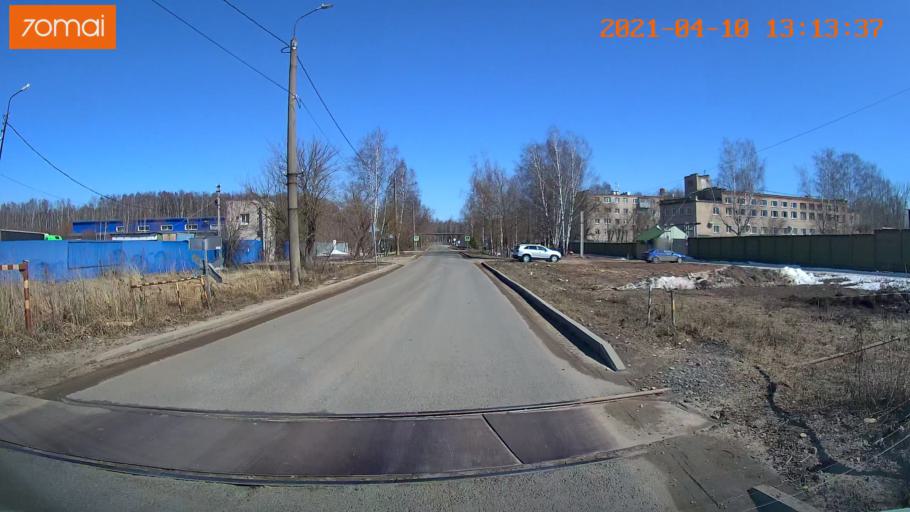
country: RU
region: Ivanovo
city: Bogorodskoye
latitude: 56.9963
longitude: 41.0464
